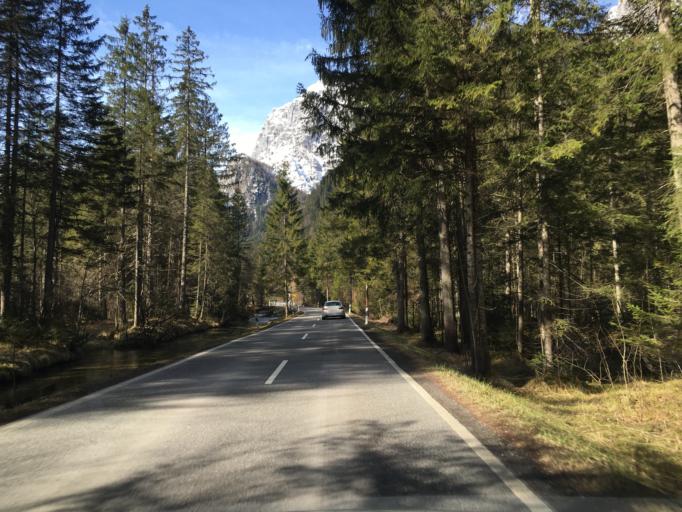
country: DE
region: Bavaria
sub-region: Upper Bavaria
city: Ramsau
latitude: 47.6026
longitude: 12.8499
